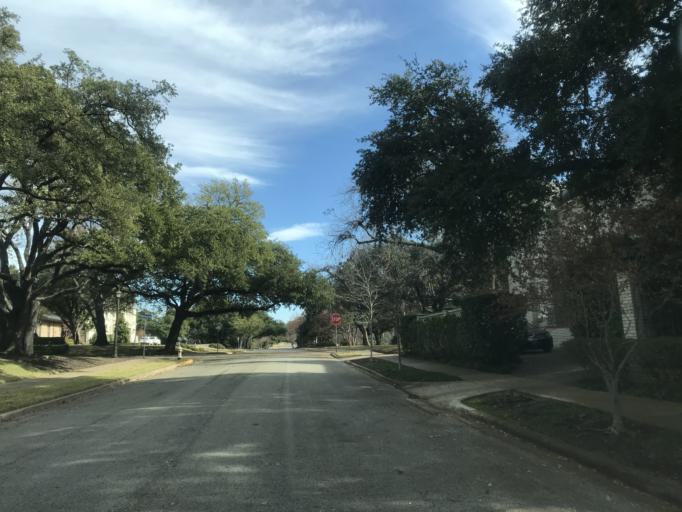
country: US
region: Texas
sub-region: Dallas County
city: Highland Park
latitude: 32.8267
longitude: -96.8000
